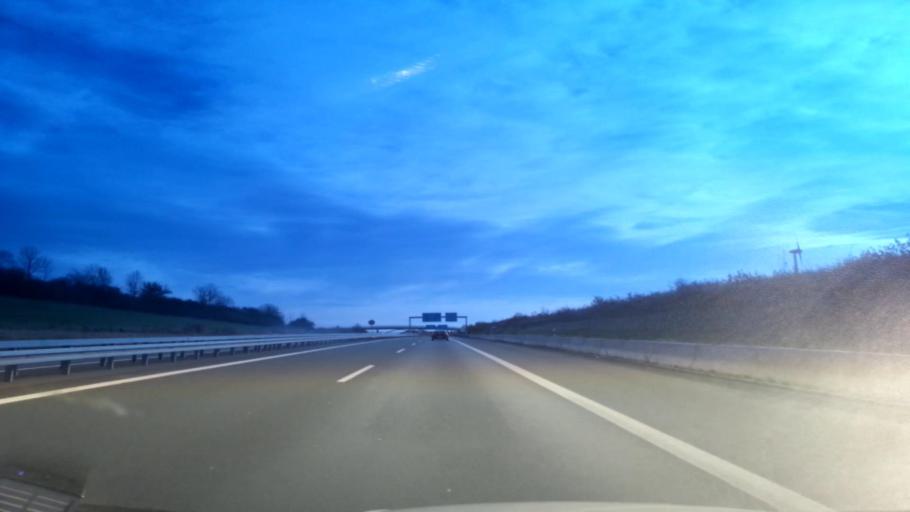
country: DE
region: Bavaria
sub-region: Upper Franconia
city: Harsdorf
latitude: 50.0269
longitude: 11.5949
